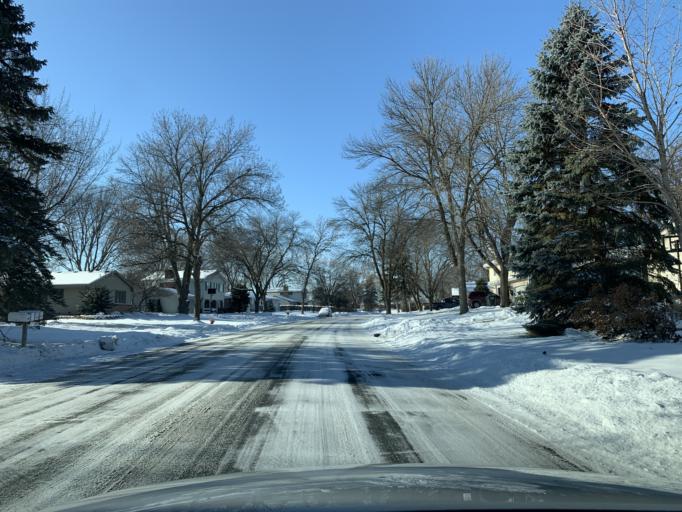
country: US
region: Minnesota
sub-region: Scott County
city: Savage
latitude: 44.8234
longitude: -93.3437
